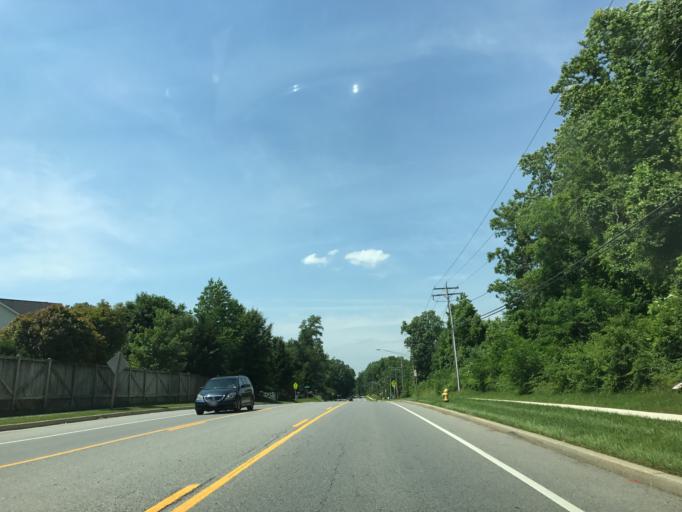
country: US
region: Maryland
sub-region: Anne Arundel County
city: Crofton
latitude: 38.9958
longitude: -76.6718
